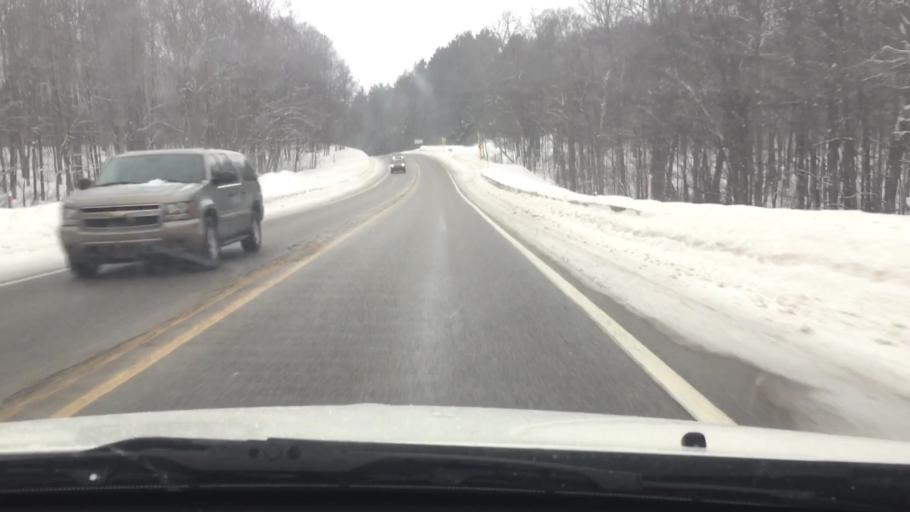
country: US
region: Michigan
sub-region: Otsego County
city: Gaylord
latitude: 45.0612
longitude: -84.7992
